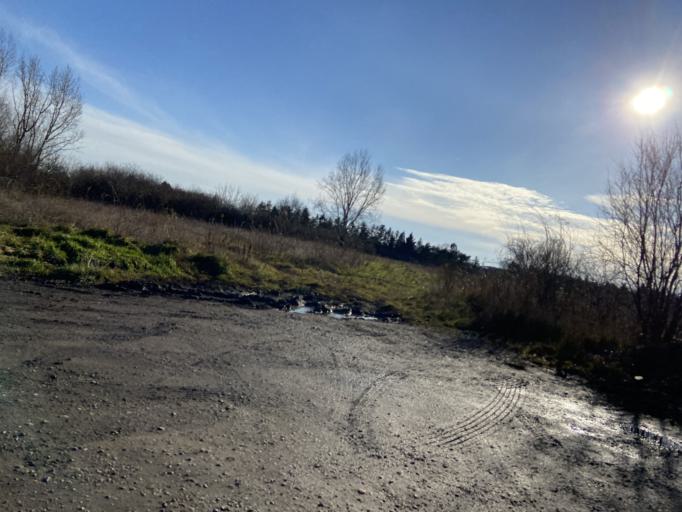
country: AT
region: Lower Austria
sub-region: Politischer Bezirk Modling
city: Neu-Guntramsdorf
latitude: 48.0607
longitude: 16.3297
